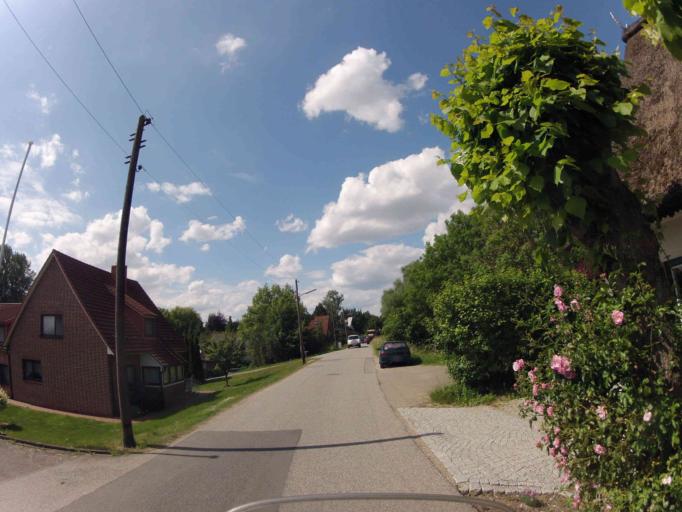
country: DE
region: Hamburg
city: Rothenburgsort
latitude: 53.4831
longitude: 10.0837
